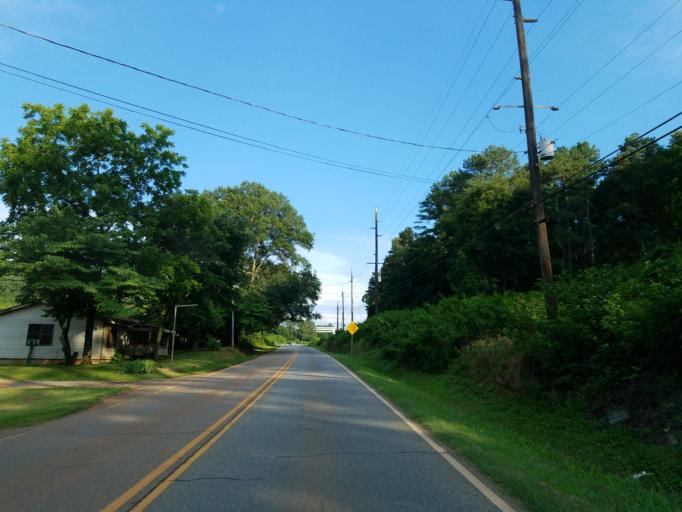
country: US
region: Georgia
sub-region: Bartow County
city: Emerson
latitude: 34.1386
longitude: -84.7628
